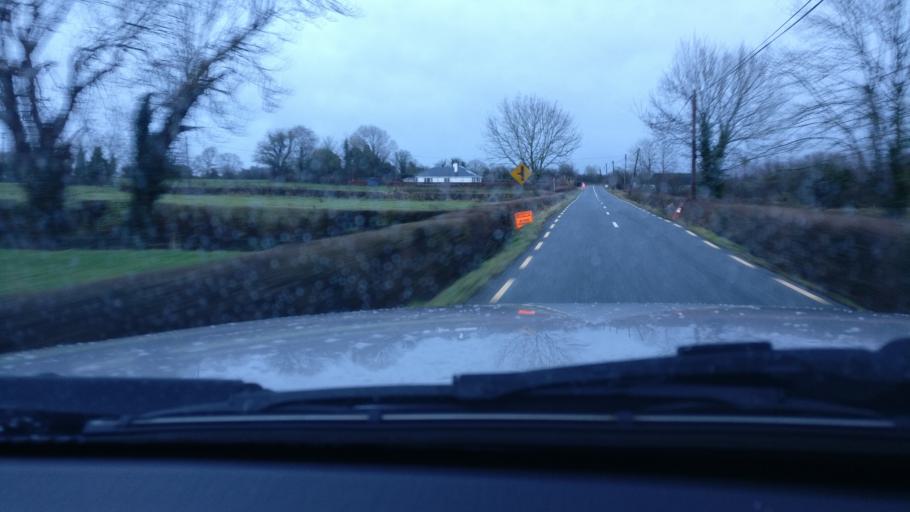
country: IE
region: Connaught
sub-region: County Galway
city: Ballinasloe
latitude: 53.2294
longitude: -8.3138
